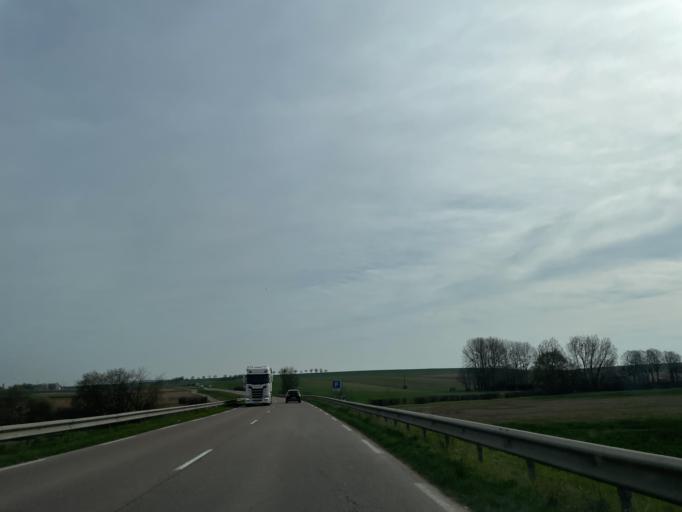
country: FR
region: Champagne-Ardenne
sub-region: Departement de l'Aube
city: Nogent-sur-Seine
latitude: 48.4823
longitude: 3.4992
